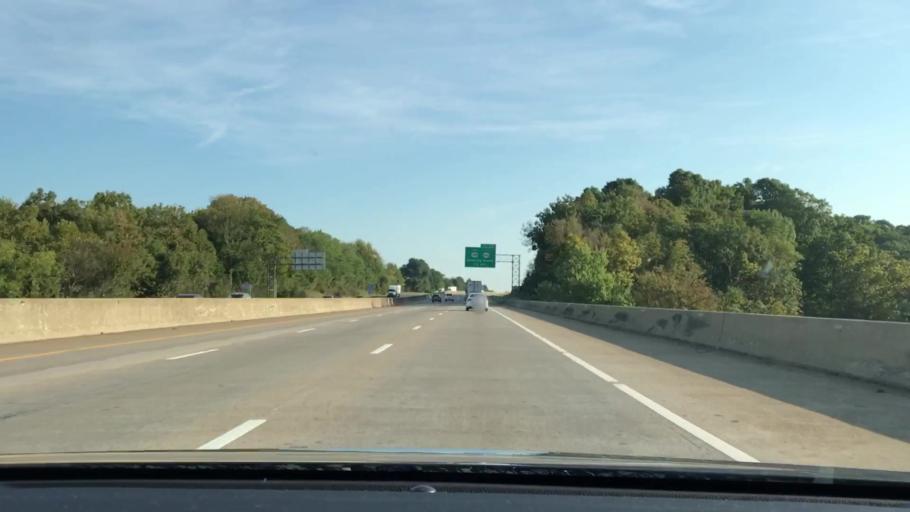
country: US
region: Kentucky
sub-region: Warren County
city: Bowling Green
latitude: 36.9883
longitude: -86.3852
